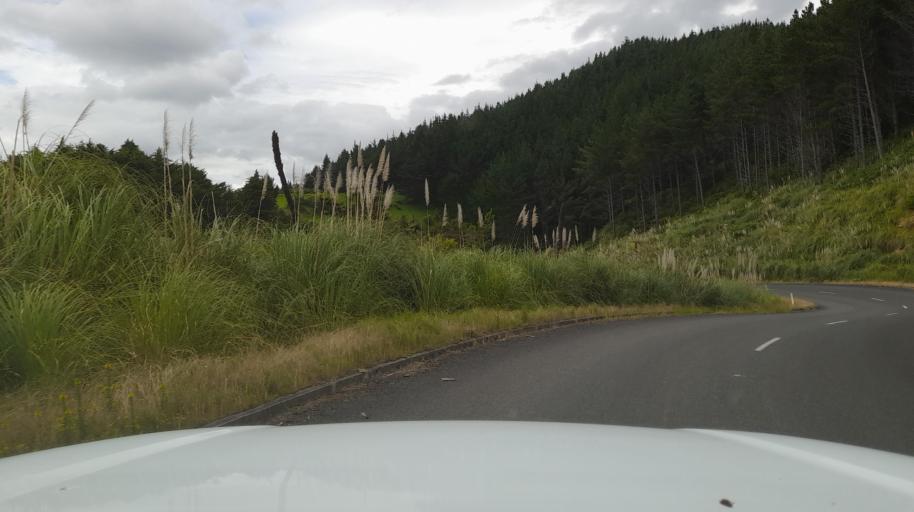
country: NZ
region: Northland
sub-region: Far North District
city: Kaitaia
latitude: -35.3666
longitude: 173.4328
